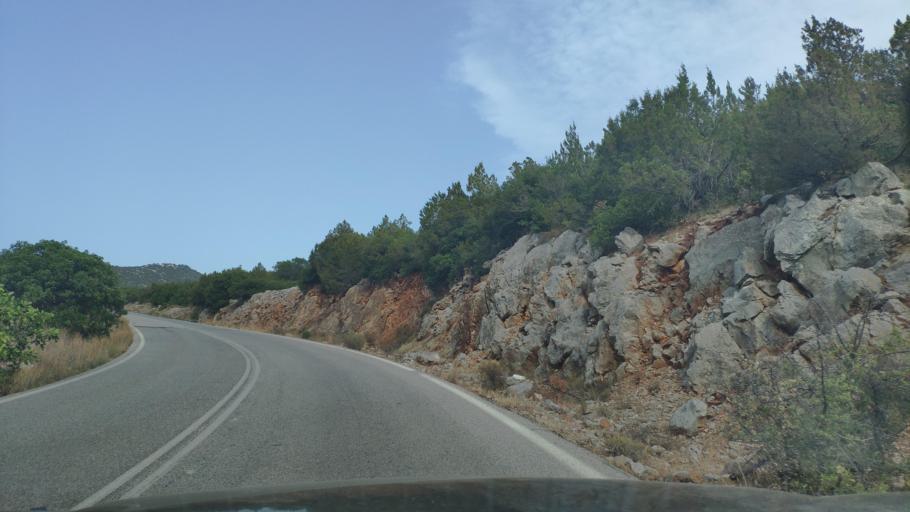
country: GR
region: Peloponnese
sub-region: Nomos Argolidos
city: Didyma
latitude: 37.5101
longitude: 23.1958
